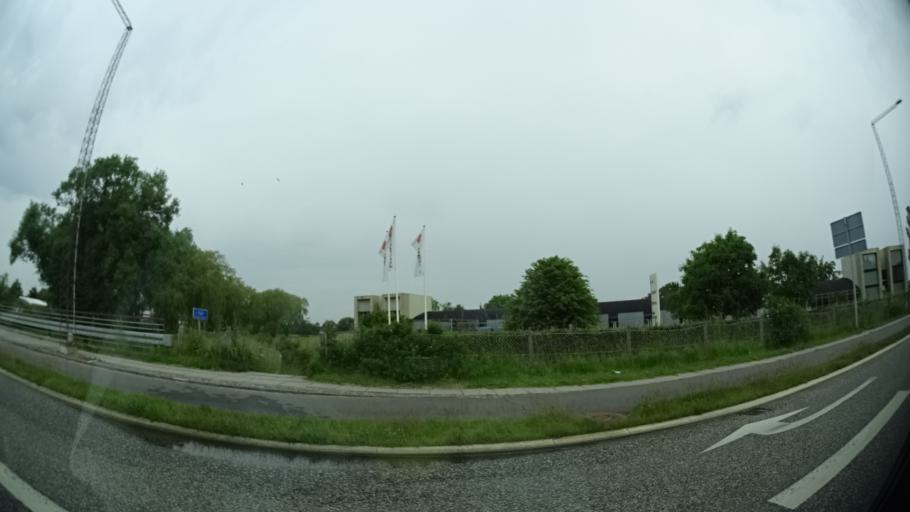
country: DK
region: Central Jutland
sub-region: Arhus Kommune
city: Lystrup
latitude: 56.2041
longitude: 10.2563
